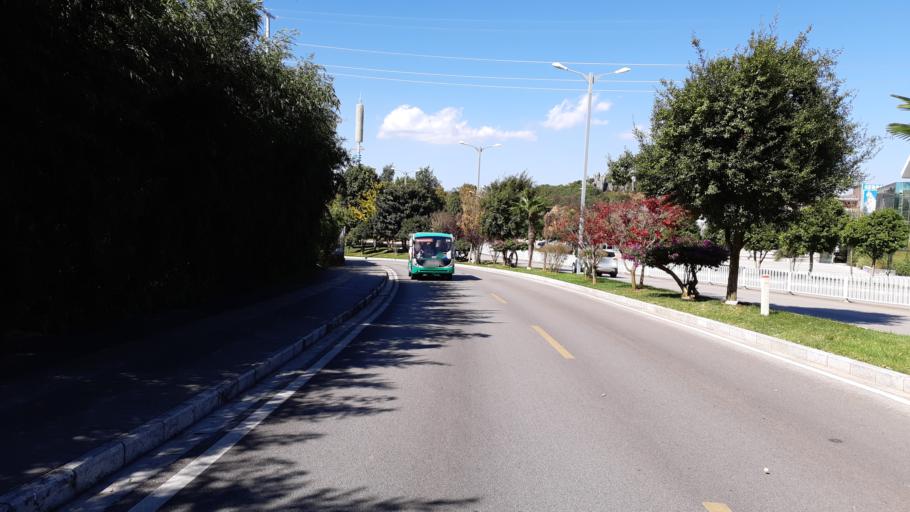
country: CN
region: Yunnan
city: Shilin
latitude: 24.8394
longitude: 103.3307
